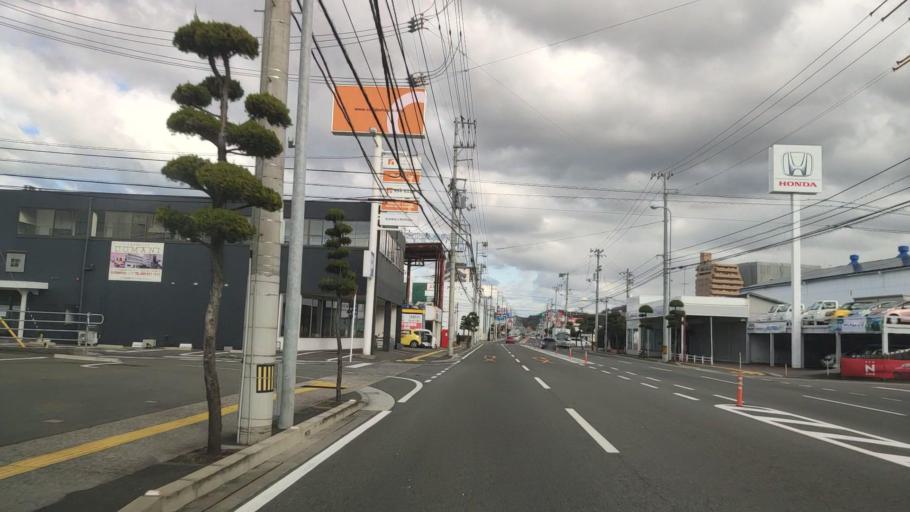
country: JP
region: Ehime
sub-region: Shikoku-chuo Shi
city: Matsuyama
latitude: 33.8597
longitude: 132.7491
